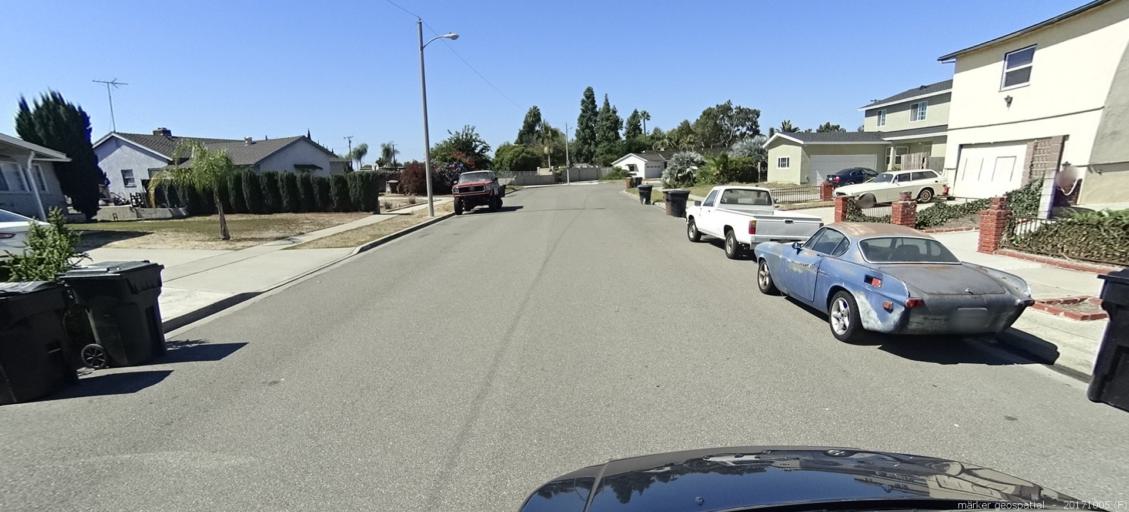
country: US
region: California
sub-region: Orange County
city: Stanton
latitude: 33.7917
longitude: -117.9691
